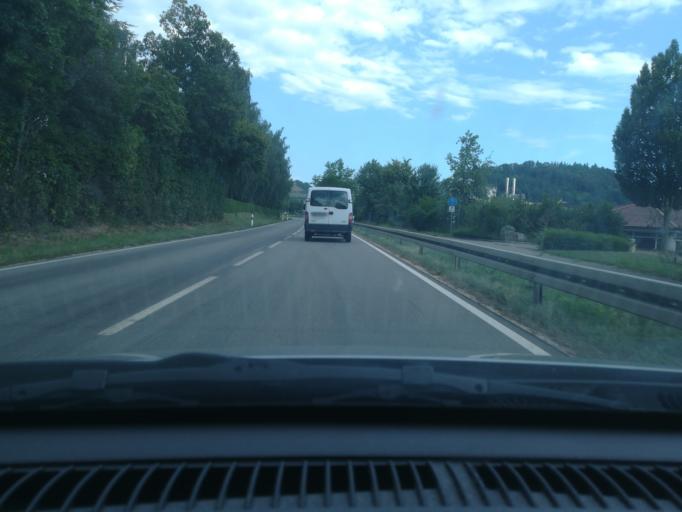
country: DE
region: Baden-Wuerttemberg
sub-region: Freiburg Region
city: Hilzingen
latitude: 47.7621
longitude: 8.7892
